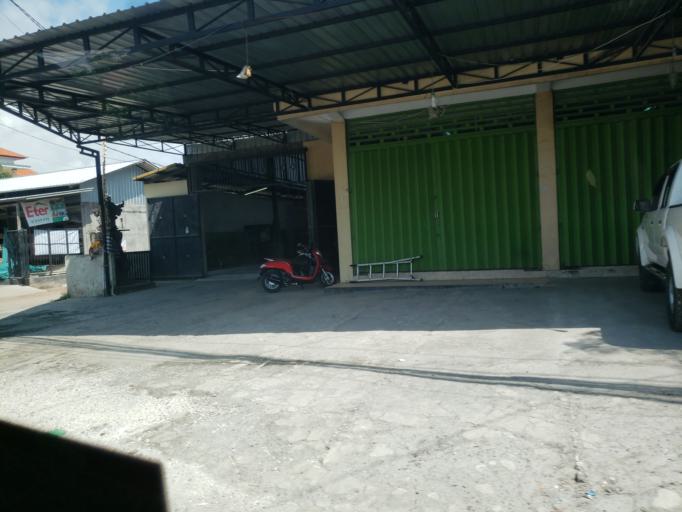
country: ID
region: Bali
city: Kangin
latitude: -8.8246
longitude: 115.1415
